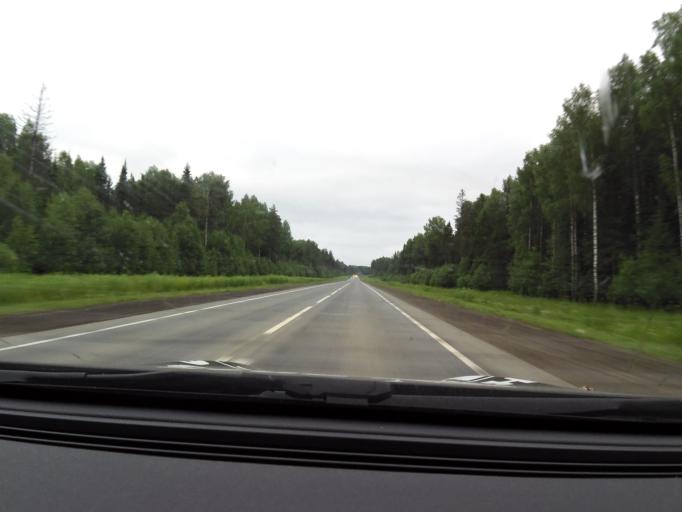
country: RU
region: Perm
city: Karagay
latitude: 58.2474
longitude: 54.9295
